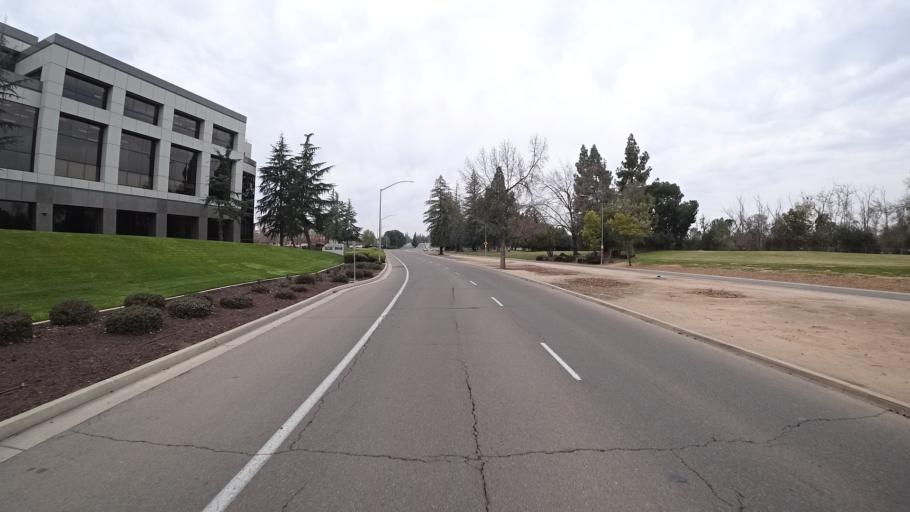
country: US
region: California
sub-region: Fresno County
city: Clovis
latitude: 36.8611
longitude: -119.7851
